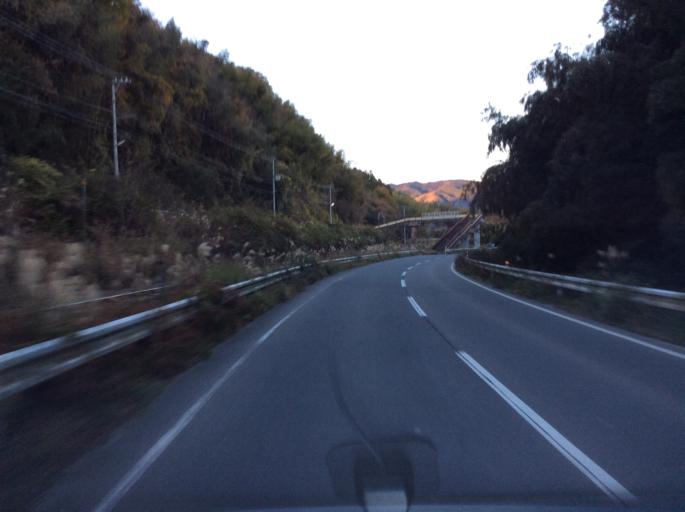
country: JP
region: Fukushima
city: Iwaki
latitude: 37.1166
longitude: 140.8597
